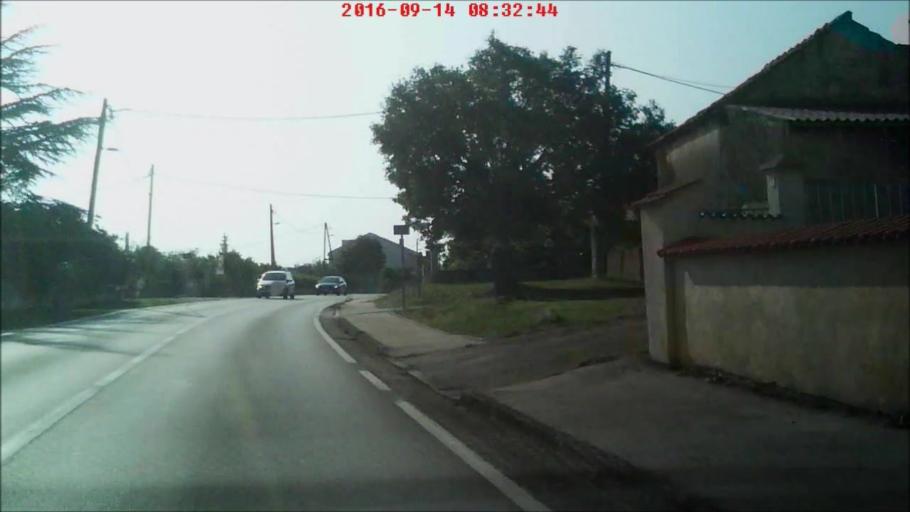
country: HR
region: Zadarska
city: Policnik
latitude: 44.1612
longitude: 15.3080
